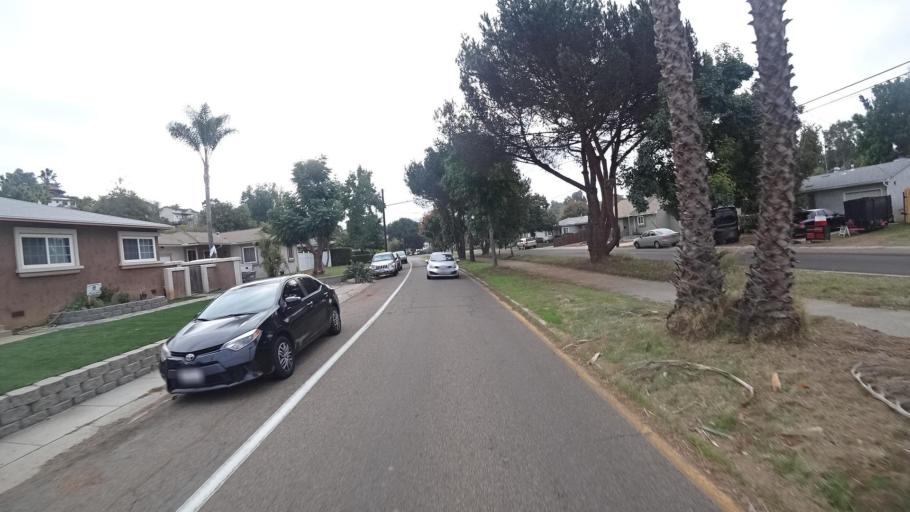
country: US
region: California
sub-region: San Diego County
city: Spring Valley
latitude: 32.7428
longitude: -117.0139
